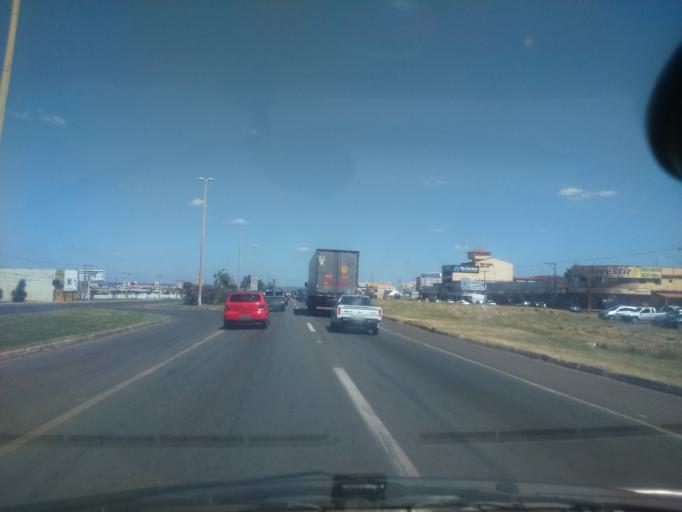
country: BR
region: Goias
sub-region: Luziania
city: Luziania
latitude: -16.0607
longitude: -47.9833
